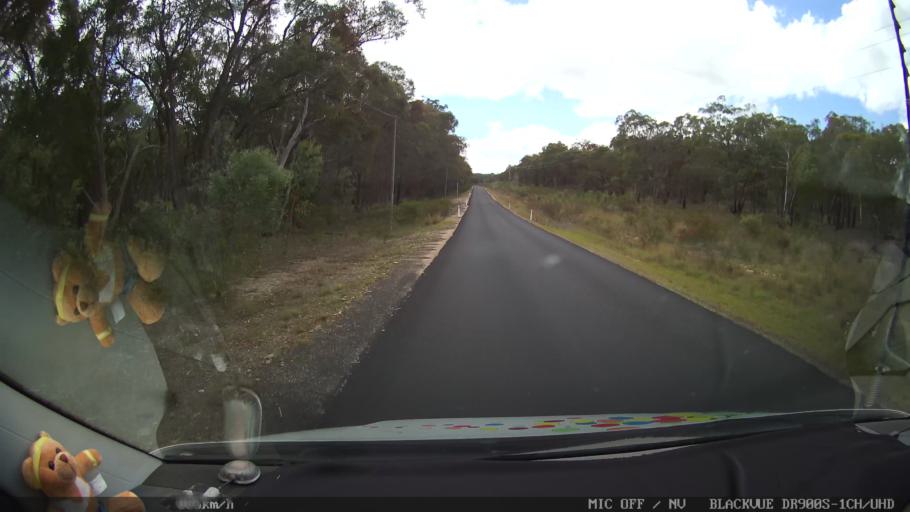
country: AU
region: New South Wales
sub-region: Glen Innes Severn
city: Glen Innes
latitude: -29.4399
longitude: 151.6206
